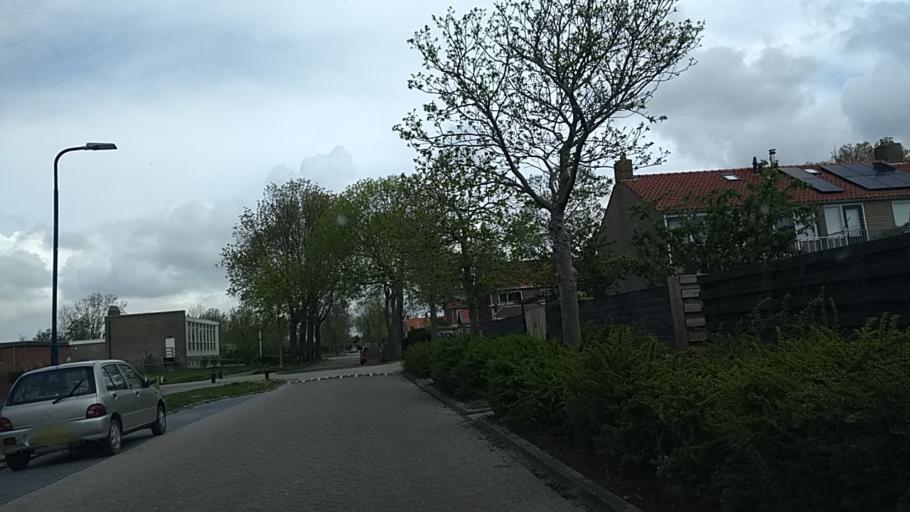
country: NL
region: Friesland
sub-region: Gemeente Harlingen
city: Harlingen
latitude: 53.1664
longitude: 5.4355
